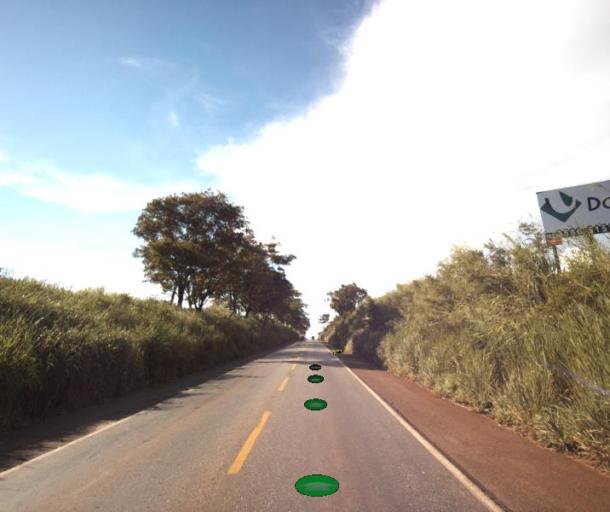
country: BR
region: Goias
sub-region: Rialma
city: Rialma
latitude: -15.3431
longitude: -49.5690
